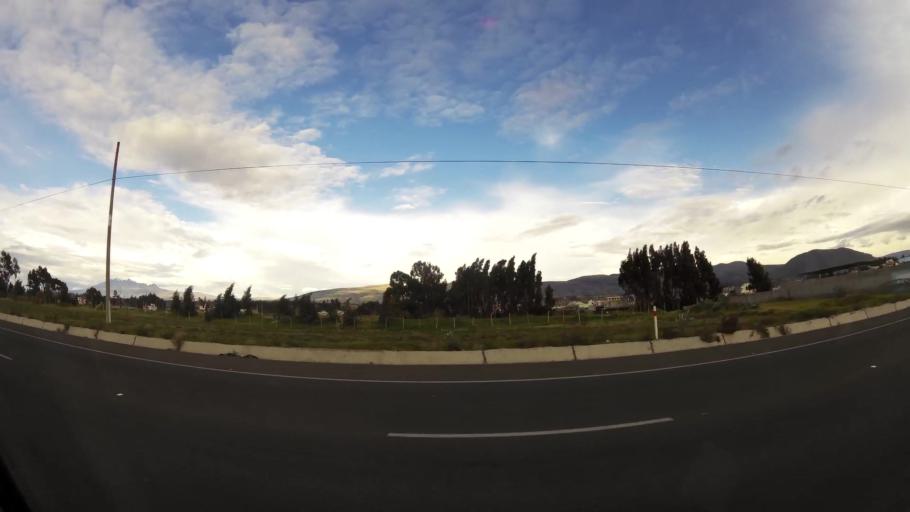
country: EC
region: Cotopaxi
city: Latacunga
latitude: -0.9102
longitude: -78.6279
